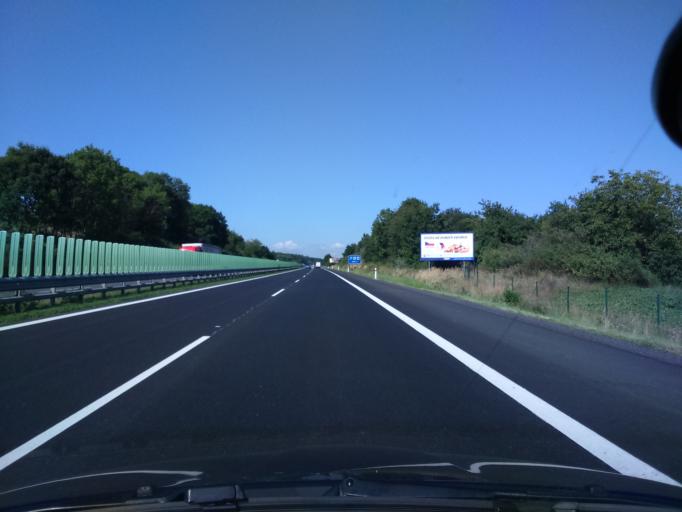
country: CZ
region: Central Bohemia
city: Poricany
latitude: 50.1282
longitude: 14.8984
